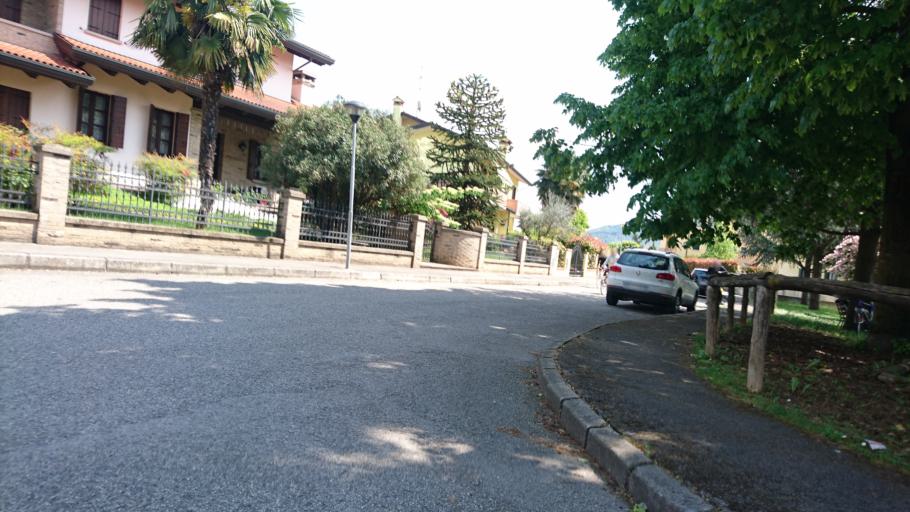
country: IT
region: Veneto
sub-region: Provincia di Padova
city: Montemerlo
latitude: 45.3802
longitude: 11.7062
